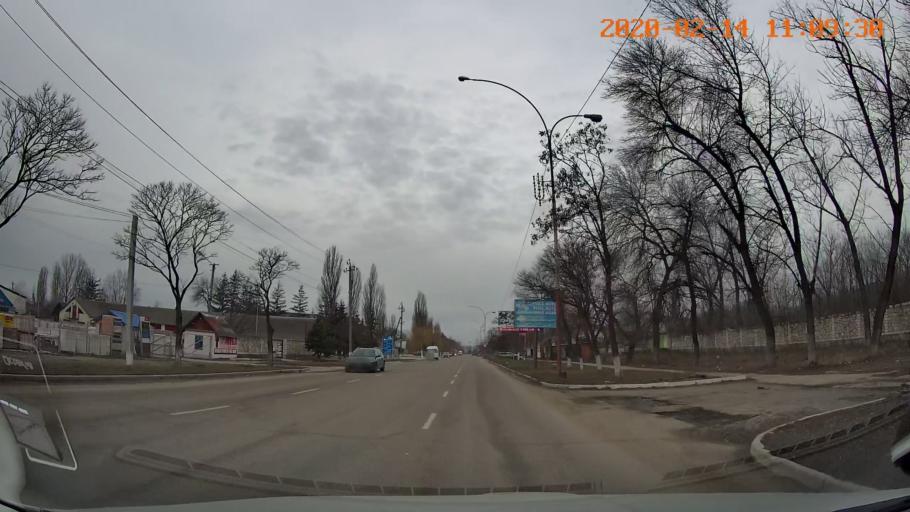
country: MD
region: Raionul Edinet
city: Edinet
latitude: 48.1788
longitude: 27.2935
